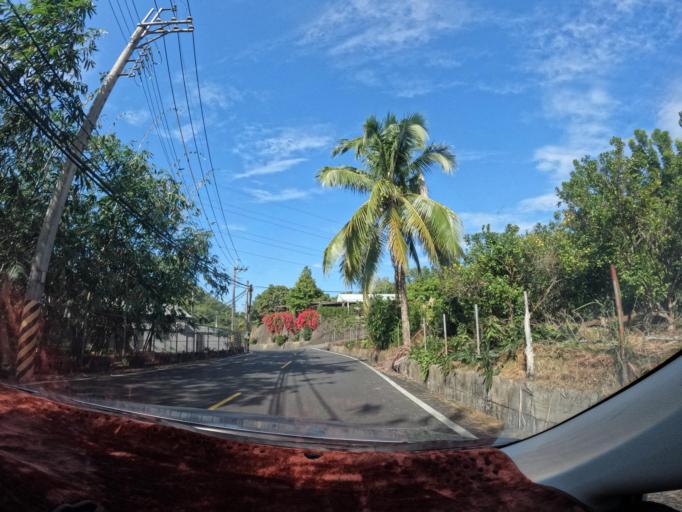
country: TW
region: Taiwan
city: Yujing
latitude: 23.0127
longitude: 120.3983
